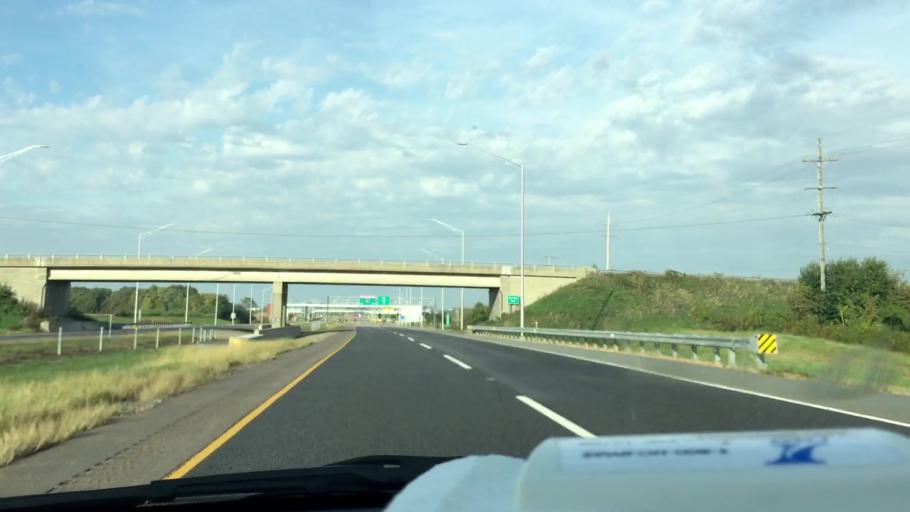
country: US
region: Illinois
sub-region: Lee County
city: Dixon
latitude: 41.8237
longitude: -89.4188
